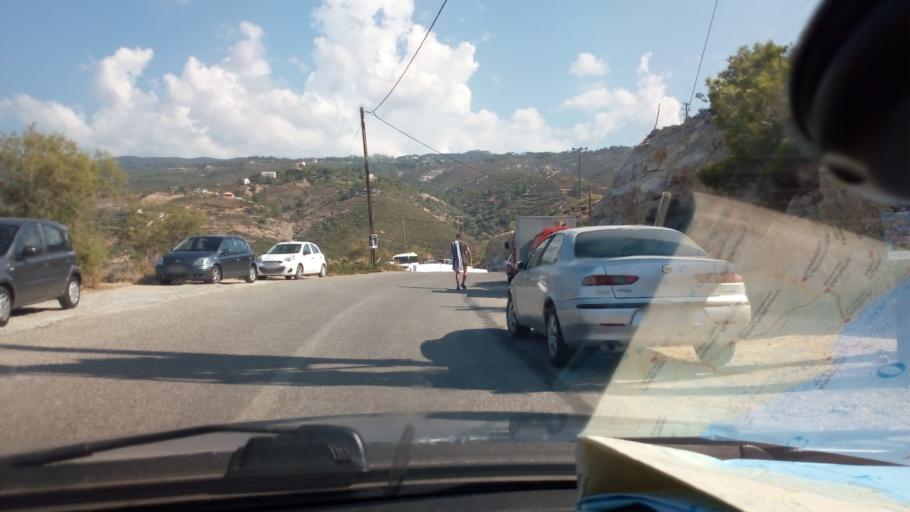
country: GR
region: North Aegean
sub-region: Nomos Samou
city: Agios Kirykos
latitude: 37.6321
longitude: 26.0893
